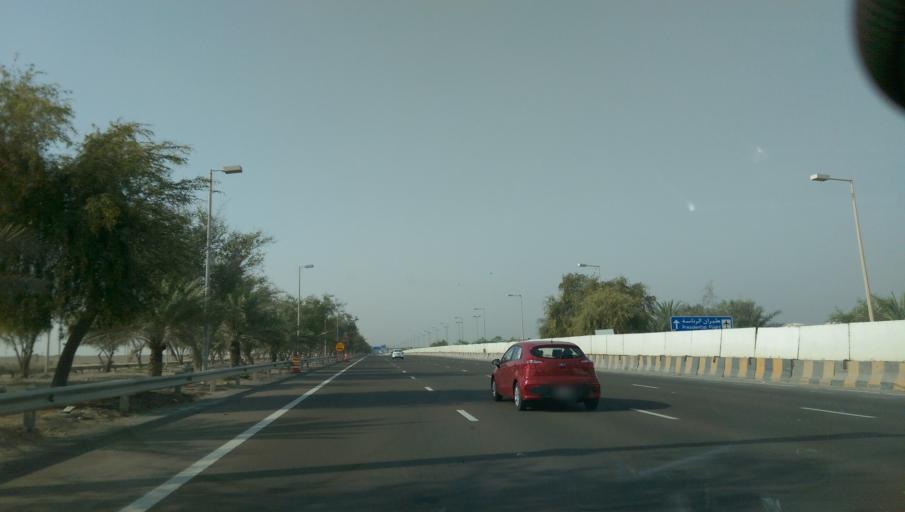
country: AE
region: Abu Dhabi
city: Abu Dhabi
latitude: 24.4397
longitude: 54.6782
